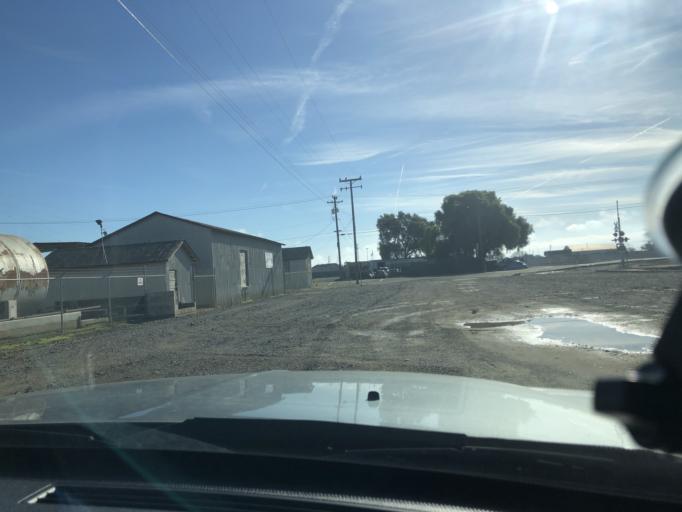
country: US
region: California
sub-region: Monterey County
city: King City
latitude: 36.2136
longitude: -121.1219
